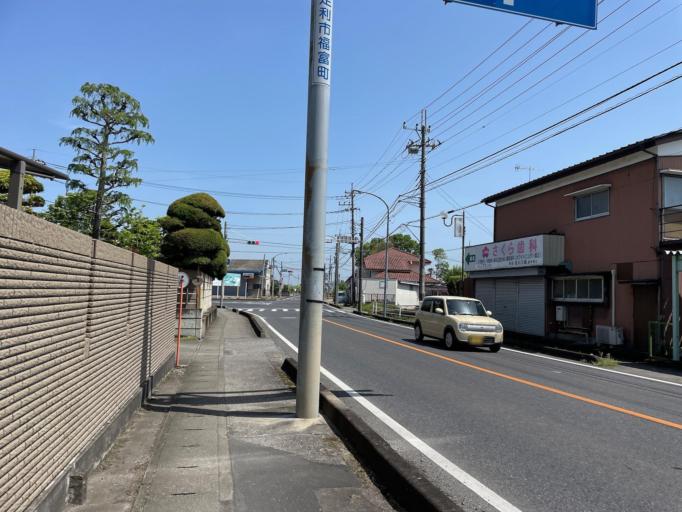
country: JP
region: Tochigi
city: Ashikaga
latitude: 36.3049
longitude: 139.4789
